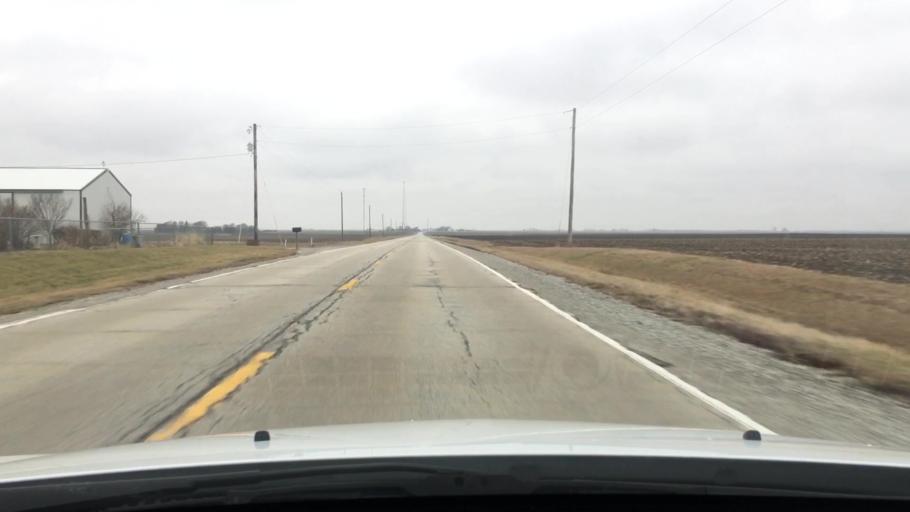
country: US
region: Illinois
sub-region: Iroquois County
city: Clifton
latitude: 40.8837
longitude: -87.9838
